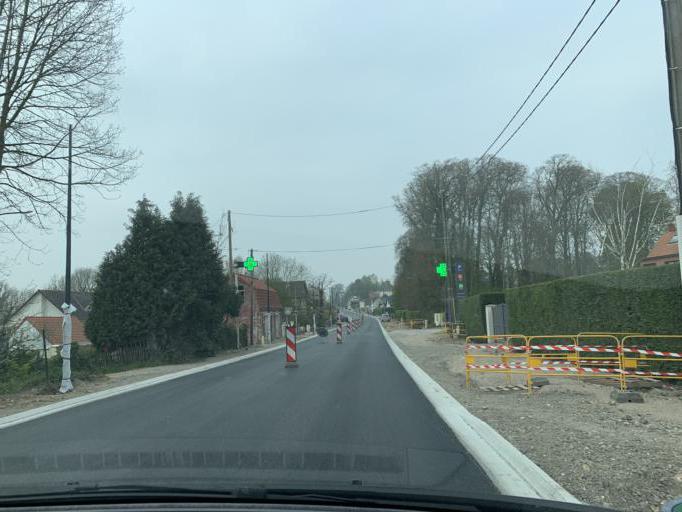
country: FR
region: Nord-Pas-de-Calais
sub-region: Departement du Pas-de-Calais
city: Montreuil
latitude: 50.4119
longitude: 1.7250
